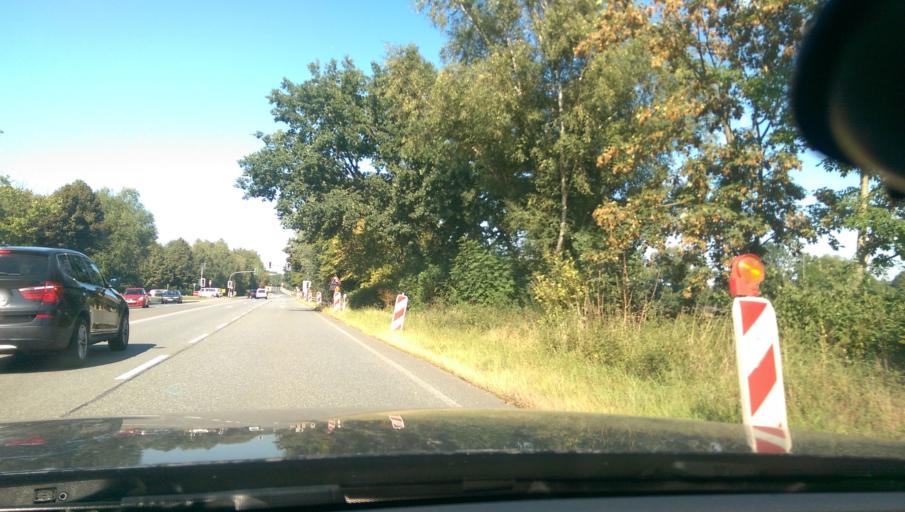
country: DE
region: Hesse
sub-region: Regierungsbezirk Kassel
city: Sontra
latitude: 51.1398
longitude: 9.9764
